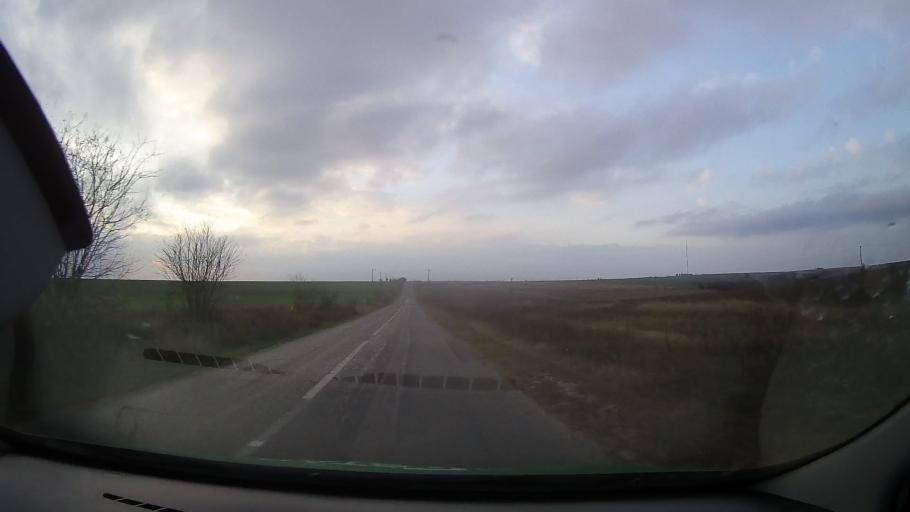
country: RO
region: Constanta
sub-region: Comuna Dobromir
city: Dobromir
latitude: 44.0329
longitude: 27.7688
